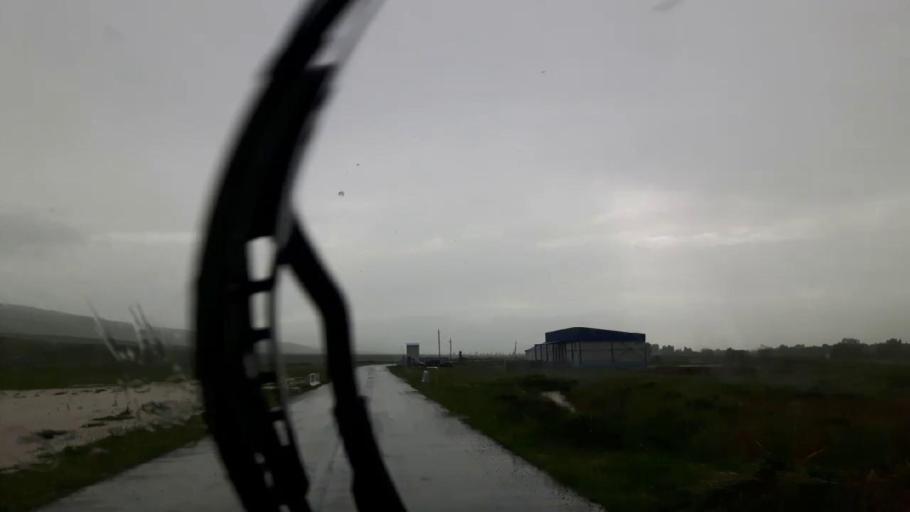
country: GE
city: Agara
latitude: 42.0148
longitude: 43.8198
